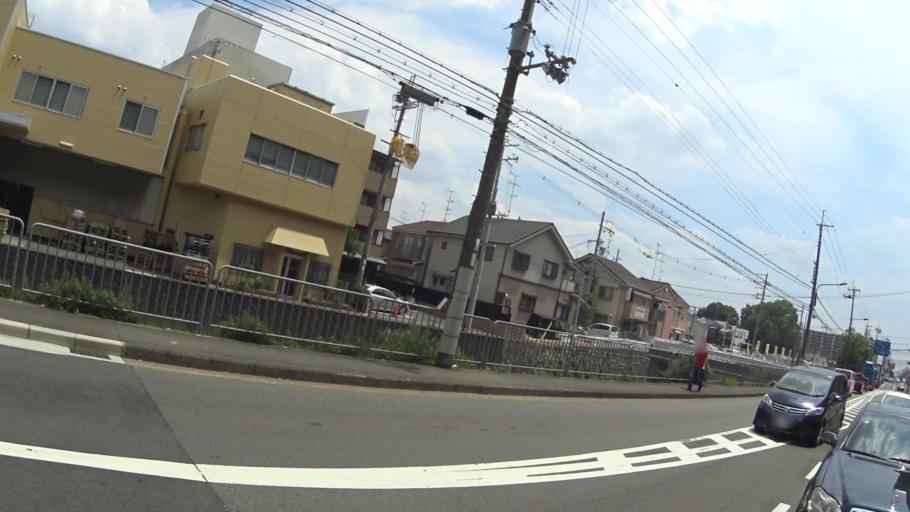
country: JP
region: Kyoto
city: Kyoto
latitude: 35.0098
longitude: 135.7165
